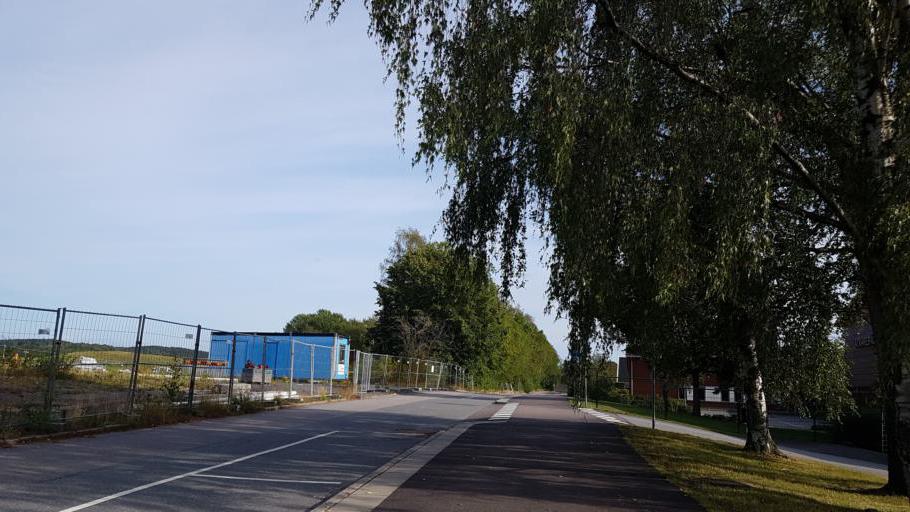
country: SE
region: Vaestra Goetaland
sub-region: Molndal
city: Moelndal
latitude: 57.6649
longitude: 12.0365
